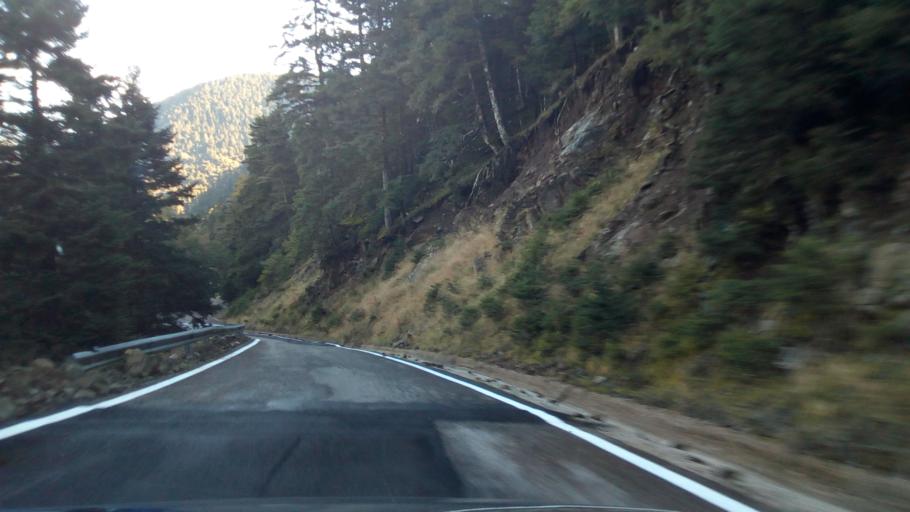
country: GR
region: West Greece
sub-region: Nomos Aitolias kai Akarnanias
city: Nafpaktos
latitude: 38.5353
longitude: 21.8467
